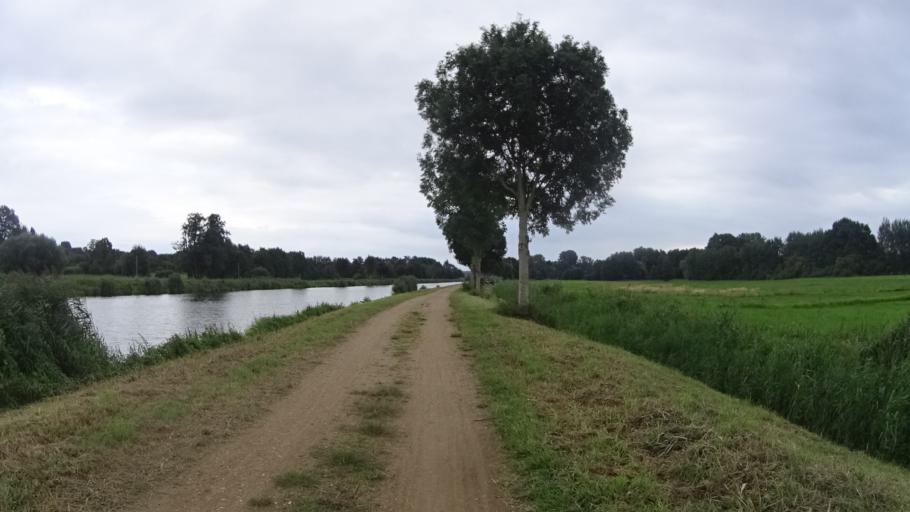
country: DE
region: Schleswig-Holstein
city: Kuhsen
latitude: 53.6806
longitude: 10.6354
